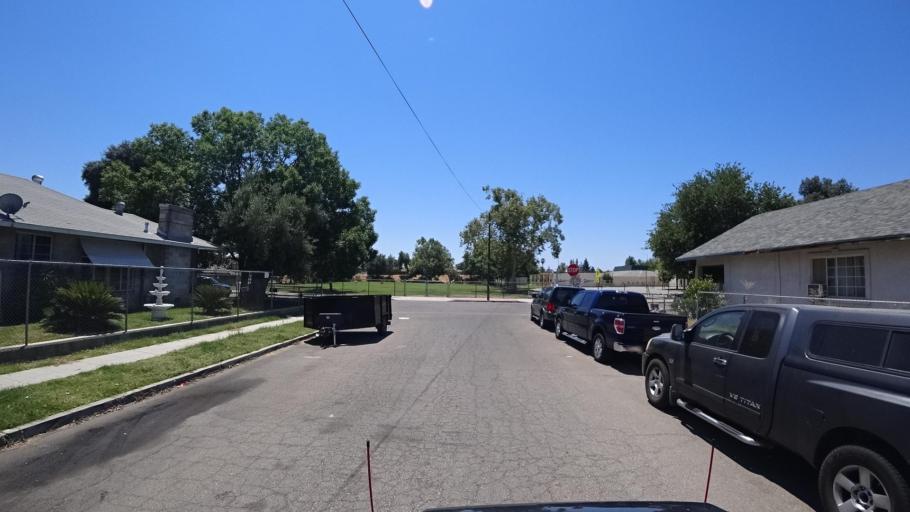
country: US
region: California
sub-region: Fresno County
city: Fresno
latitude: 36.7559
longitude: -119.7785
